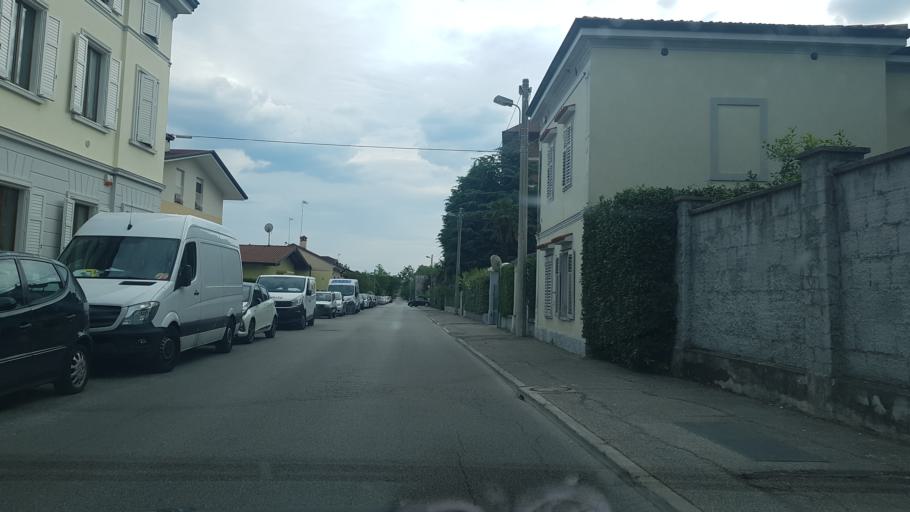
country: IT
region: Friuli Venezia Giulia
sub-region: Provincia di Gorizia
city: Gorizia
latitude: 45.9346
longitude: 13.6198
